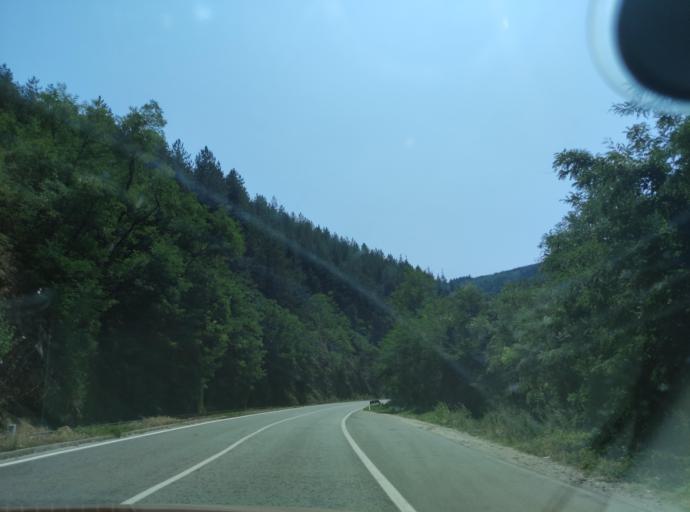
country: BG
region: Blagoevgrad
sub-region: Obshtina Belitsa
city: Belitsa
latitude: 41.8891
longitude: 23.5650
